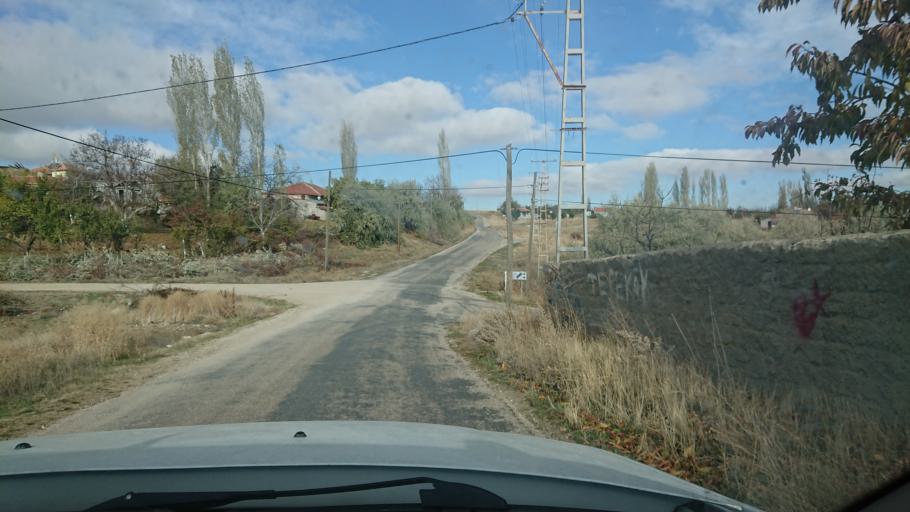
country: TR
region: Aksaray
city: Ortakoy
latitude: 38.8107
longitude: 33.9840
